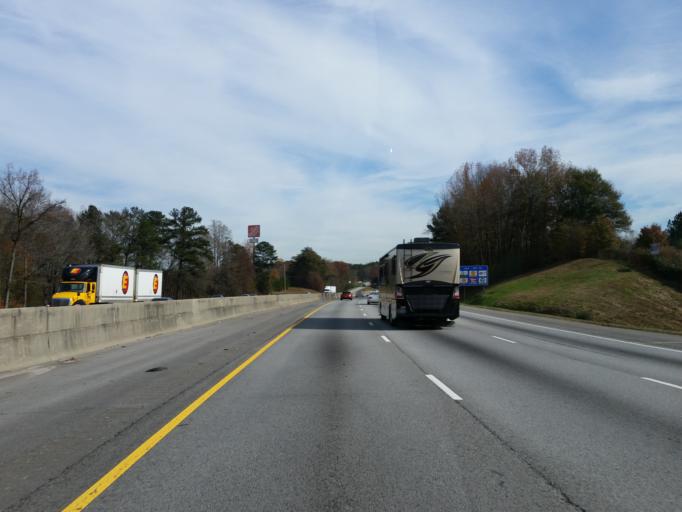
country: US
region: Georgia
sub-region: Cobb County
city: Austell
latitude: 33.7765
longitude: -84.6146
